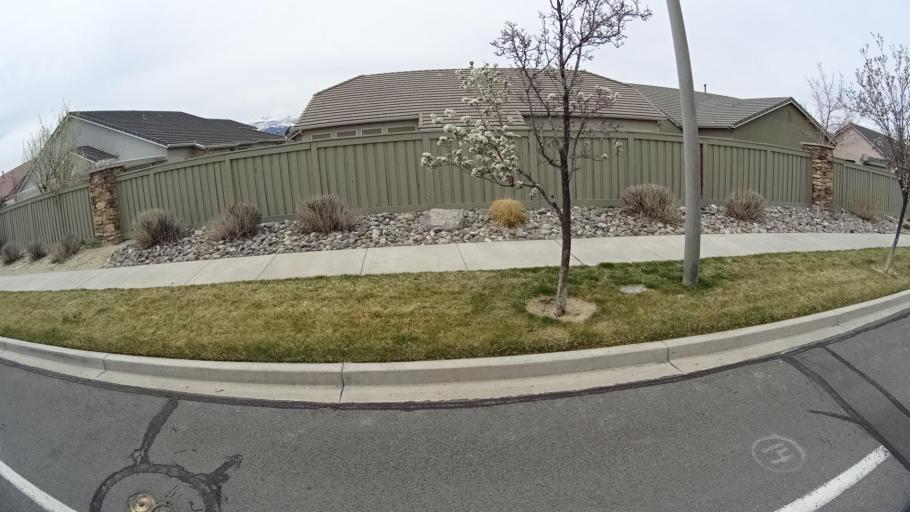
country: US
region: Nevada
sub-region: Washoe County
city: Sparks
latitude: 39.4422
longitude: -119.7360
